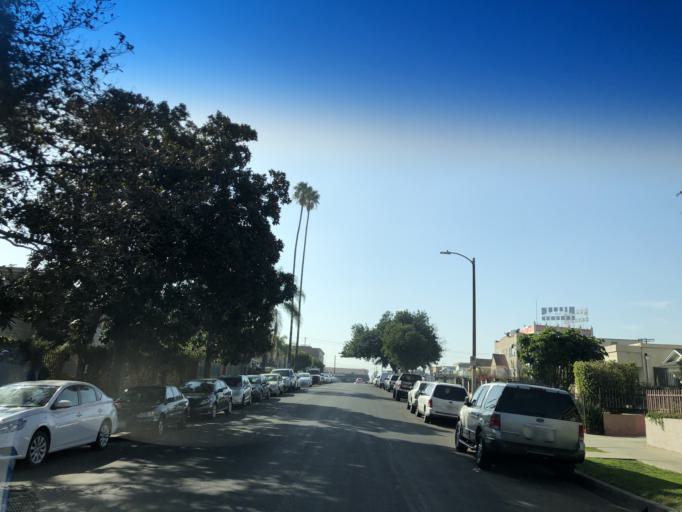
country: US
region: California
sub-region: Los Angeles County
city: Hollywood
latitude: 34.0495
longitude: -118.3245
